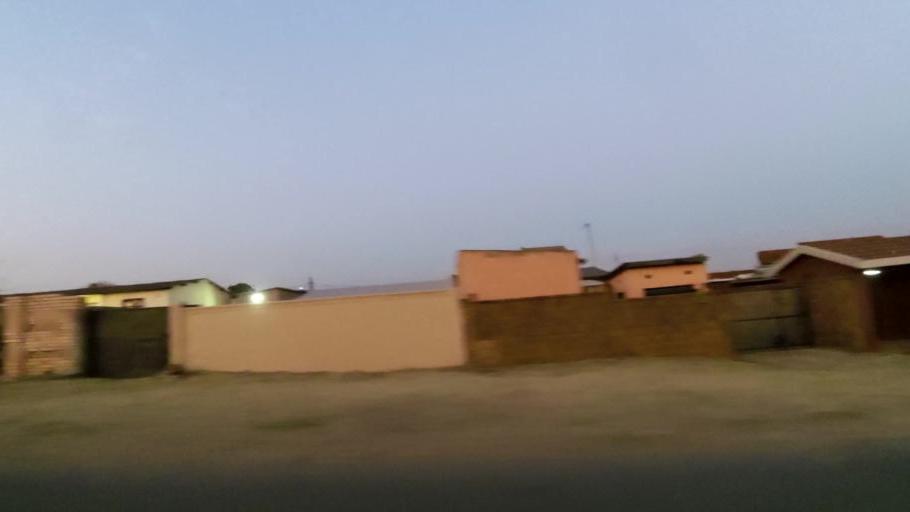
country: ZA
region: Gauteng
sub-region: City of Johannesburg Metropolitan Municipality
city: Soweto
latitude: -26.2296
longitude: 27.9116
